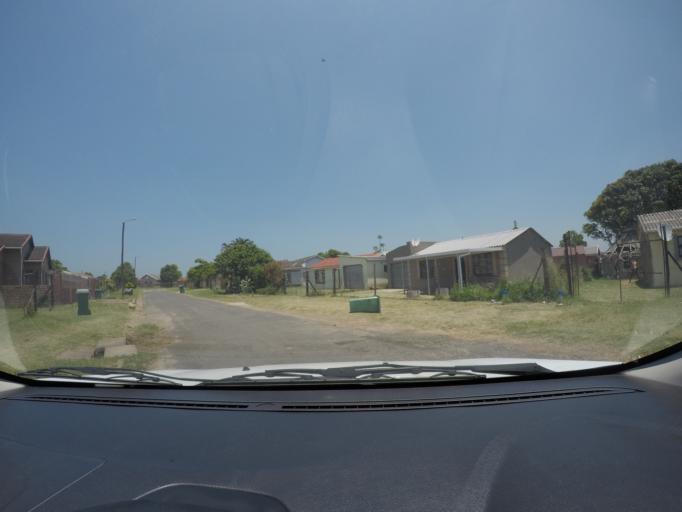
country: ZA
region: KwaZulu-Natal
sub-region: uThungulu District Municipality
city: eSikhawini
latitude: -28.8821
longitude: 31.9020
